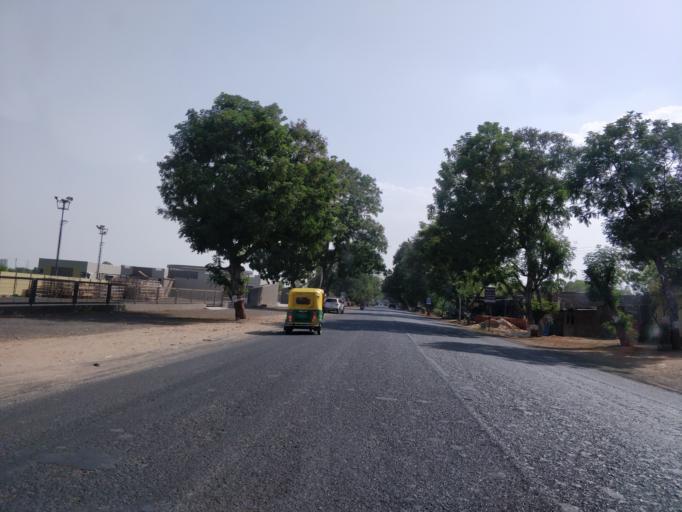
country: IN
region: Gujarat
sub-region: Ahmadabad
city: Naroda
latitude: 23.0972
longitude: 72.6994
